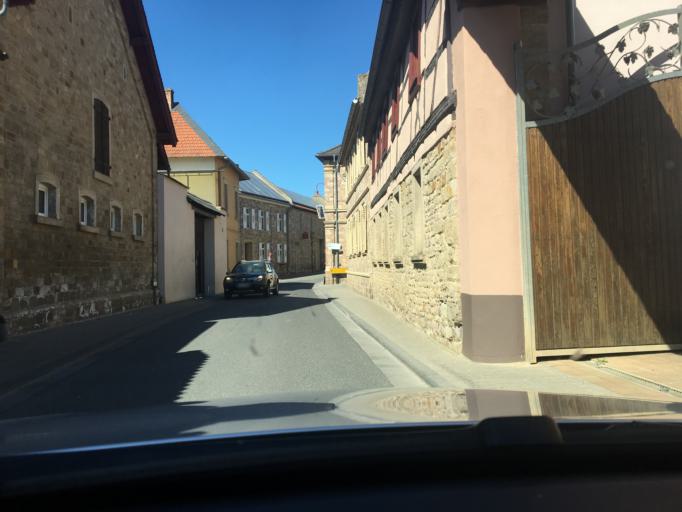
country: DE
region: Rheinland-Pfalz
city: Eckelsheim
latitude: 49.7943
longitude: 7.9836
